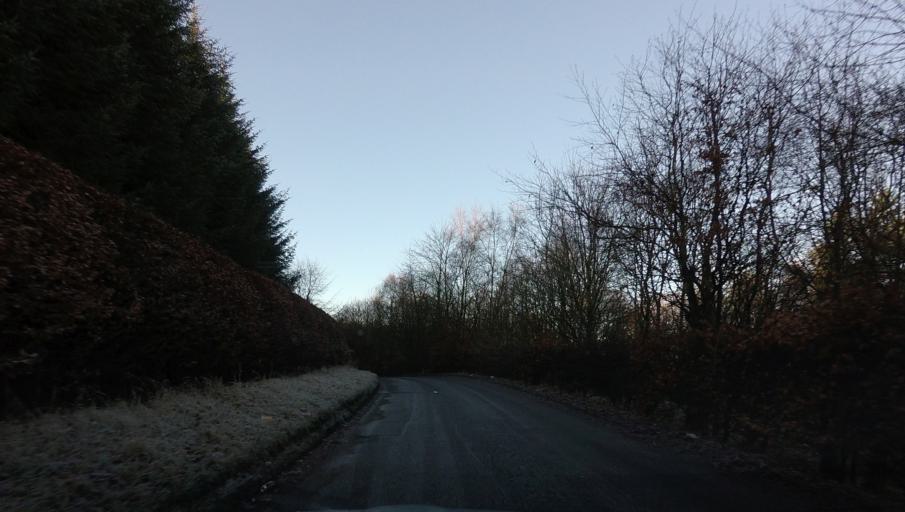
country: GB
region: Scotland
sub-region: North Lanarkshire
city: Newmains
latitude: 55.8062
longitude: -3.8557
